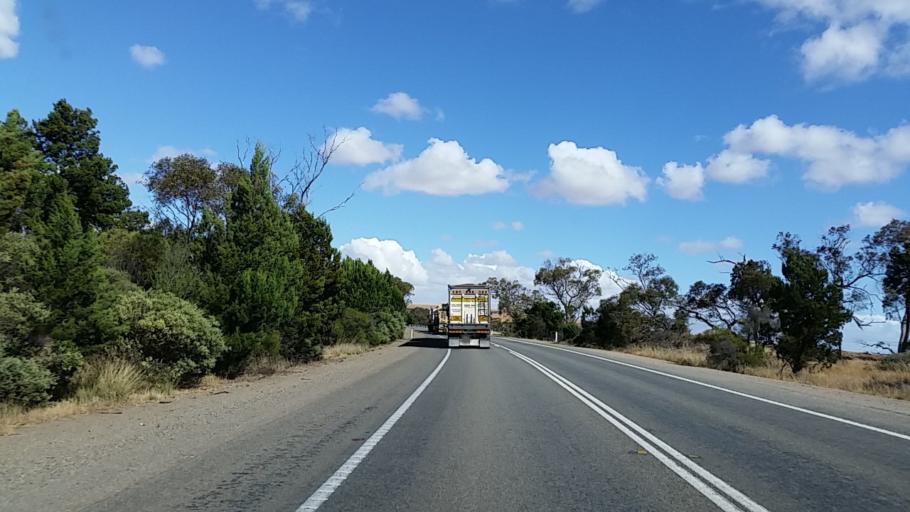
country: AU
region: South Australia
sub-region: Wakefield
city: Balaklava
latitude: -33.9483
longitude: 138.1663
